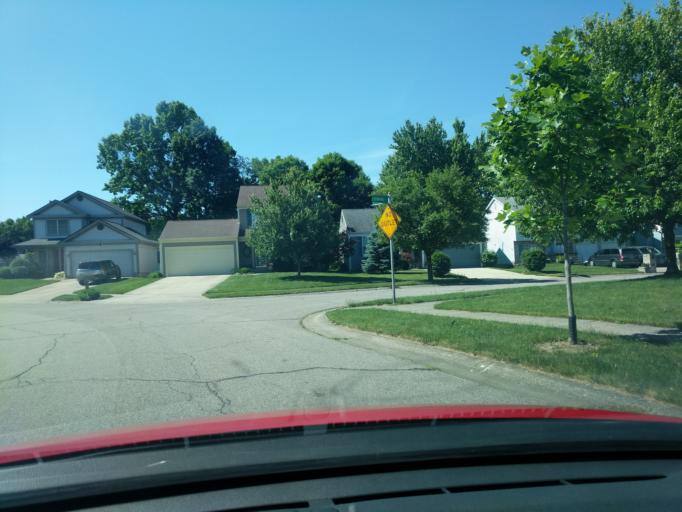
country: US
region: Ohio
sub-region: Franklin County
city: Huber Ridge
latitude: 40.0661
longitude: -82.9109
